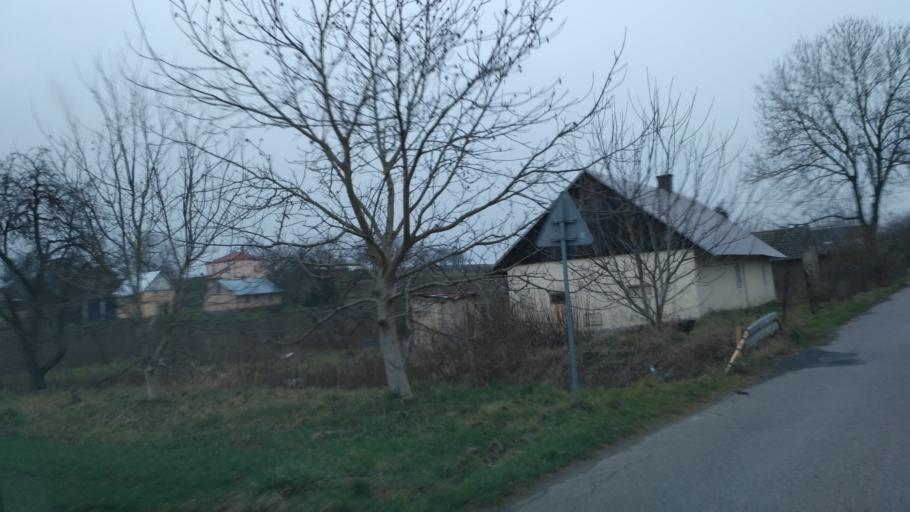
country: PL
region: Subcarpathian Voivodeship
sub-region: Powiat jaroslawski
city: Pawlosiow
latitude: 49.9680
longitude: 22.6464
